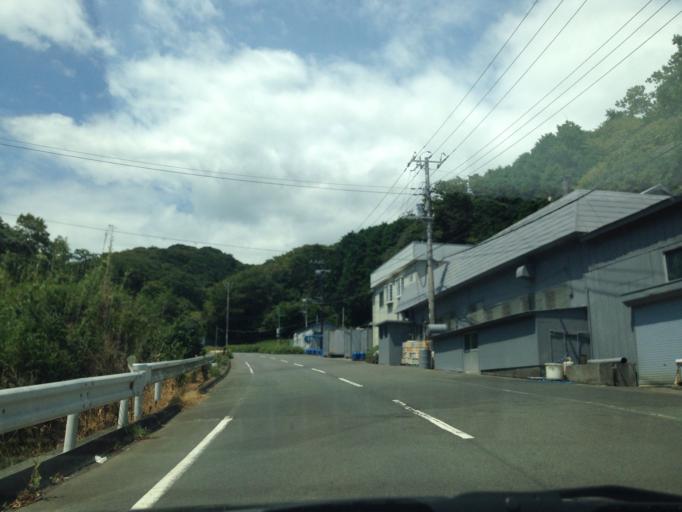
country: JP
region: Shizuoka
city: Shimoda
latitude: 34.6317
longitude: 138.8216
